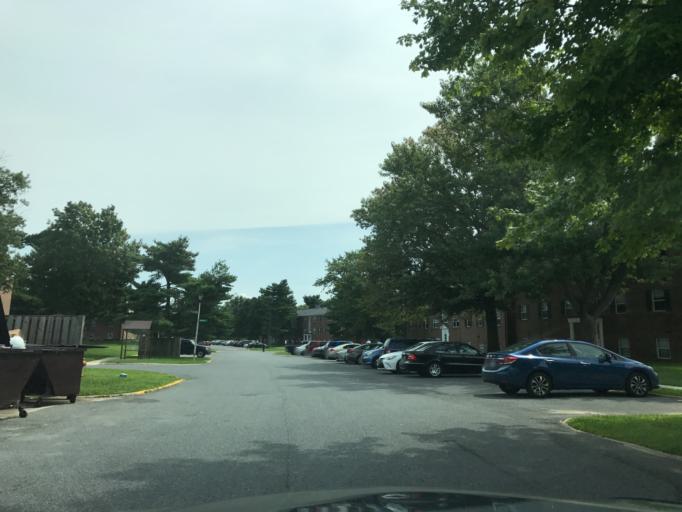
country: US
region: Maryland
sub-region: Baltimore County
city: Essex
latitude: 39.3026
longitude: -76.4492
